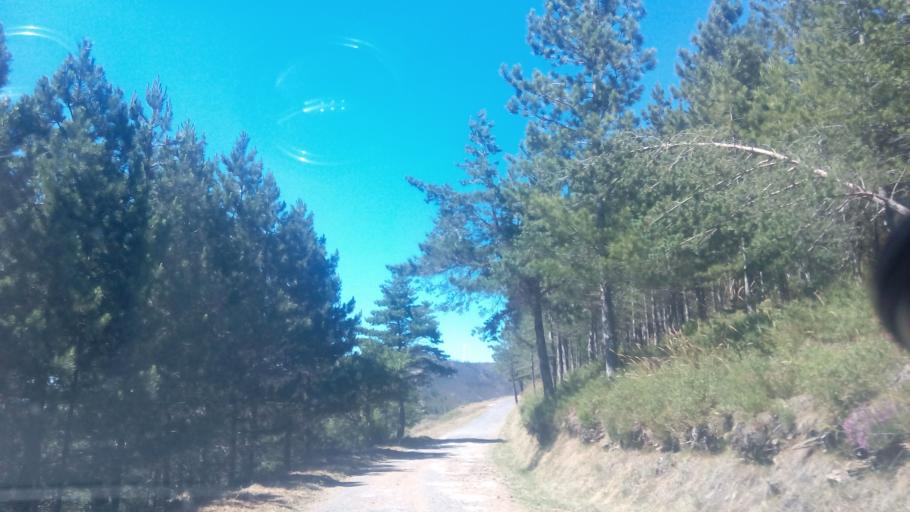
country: PT
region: Vila Real
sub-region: Mesao Frio
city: Mesao Frio
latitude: 41.2685
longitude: -7.9251
